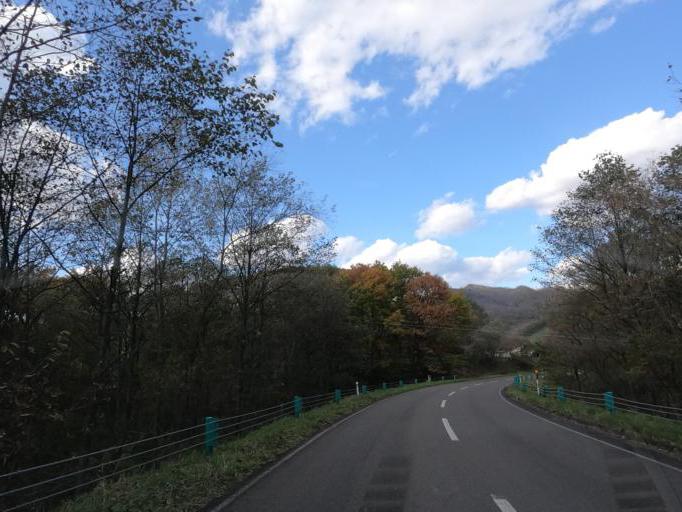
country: JP
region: Hokkaido
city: Otofuke
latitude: 43.2810
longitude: 143.2348
